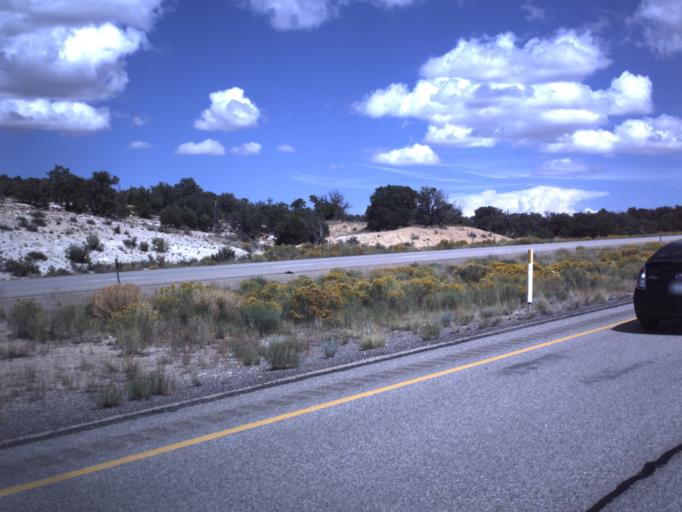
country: US
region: Utah
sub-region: Emery County
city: Ferron
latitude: 38.8589
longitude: -110.8308
